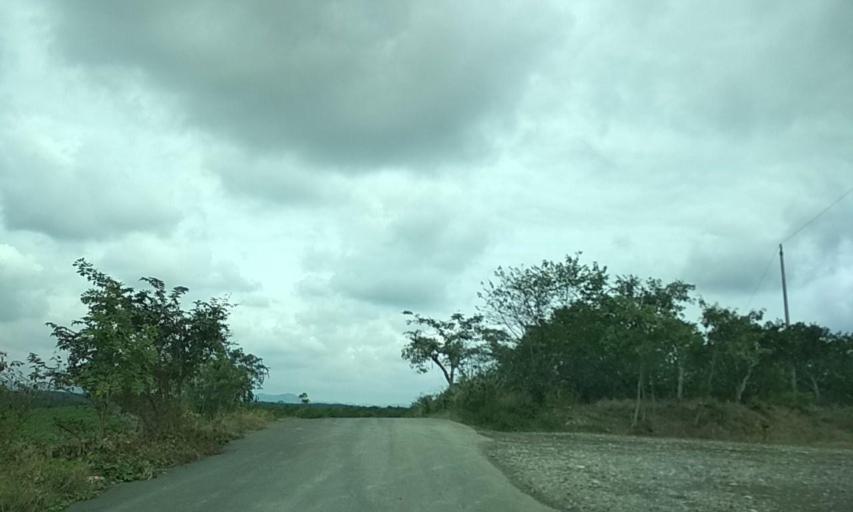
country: MX
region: Puebla
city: Espinal
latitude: 20.3309
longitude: -97.4055
